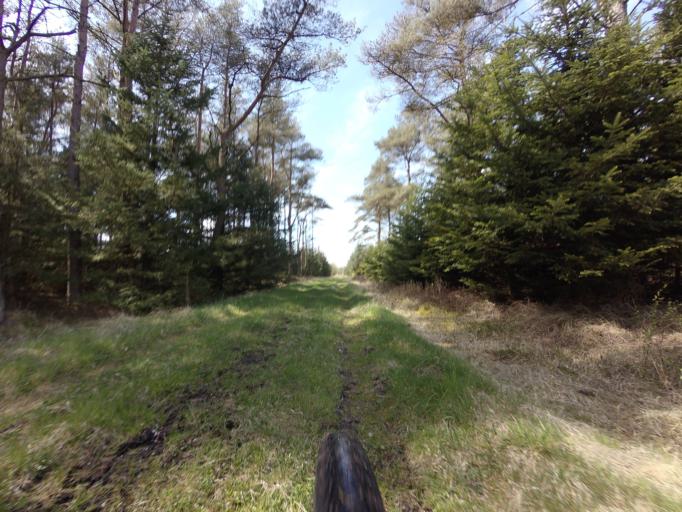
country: DK
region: North Denmark
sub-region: Jammerbugt Kommune
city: Brovst
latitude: 57.1650
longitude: 9.5482
